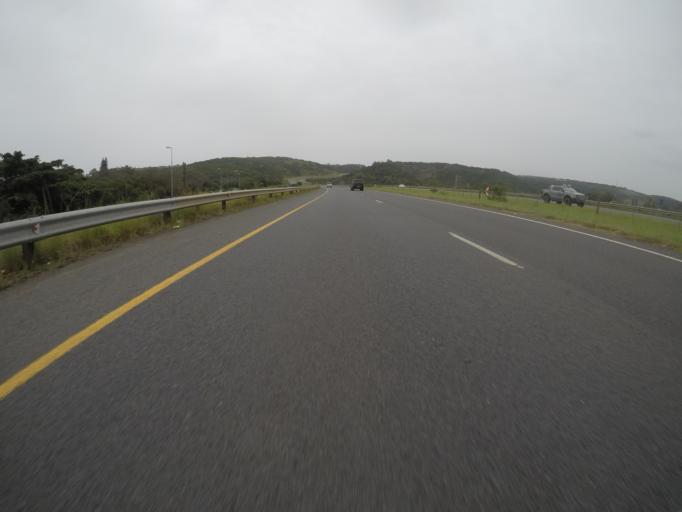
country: ZA
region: Eastern Cape
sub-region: Buffalo City Metropolitan Municipality
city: East London
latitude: -32.9630
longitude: 27.9211
